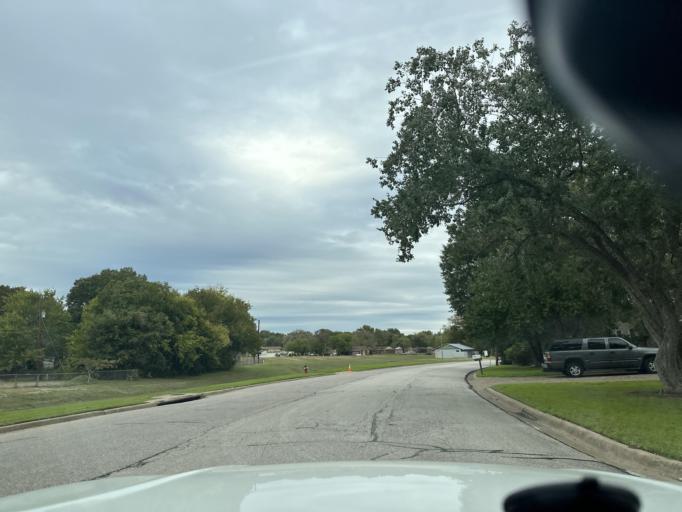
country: US
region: Texas
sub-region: Washington County
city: Brenham
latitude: 30.1678
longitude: -96.4092
